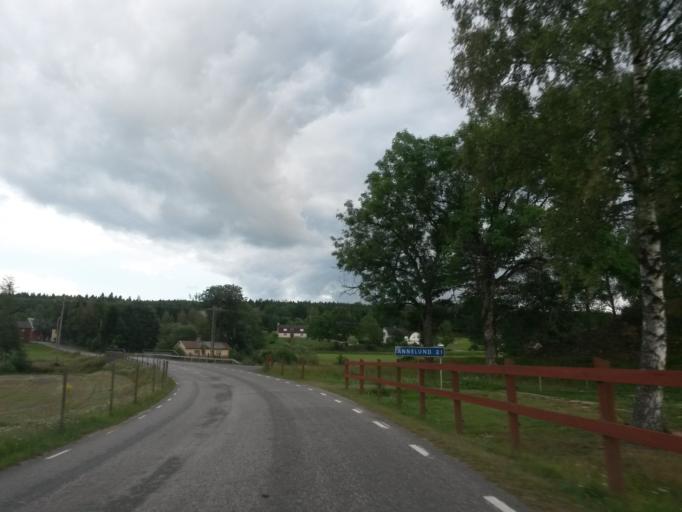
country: SE
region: Vaestra Goetaland
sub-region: Vargarda Kommun
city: Jonstorp
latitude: 57.9863
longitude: 12.7702
